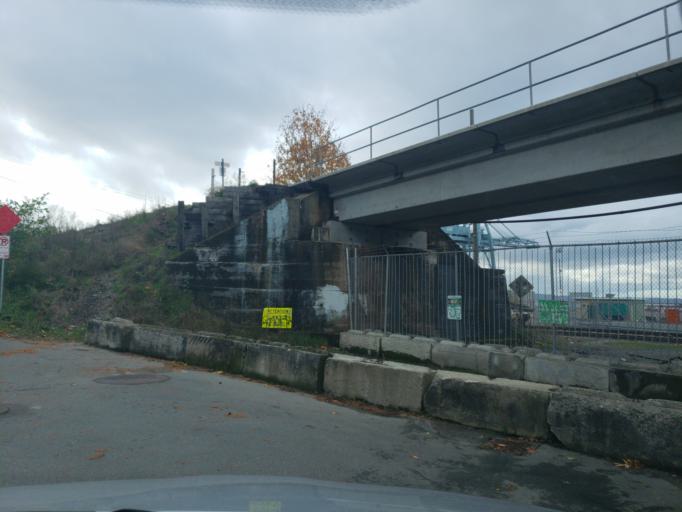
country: US
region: Washington
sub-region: Snohomish County
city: Everett
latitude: 47.9775
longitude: -122.2199
